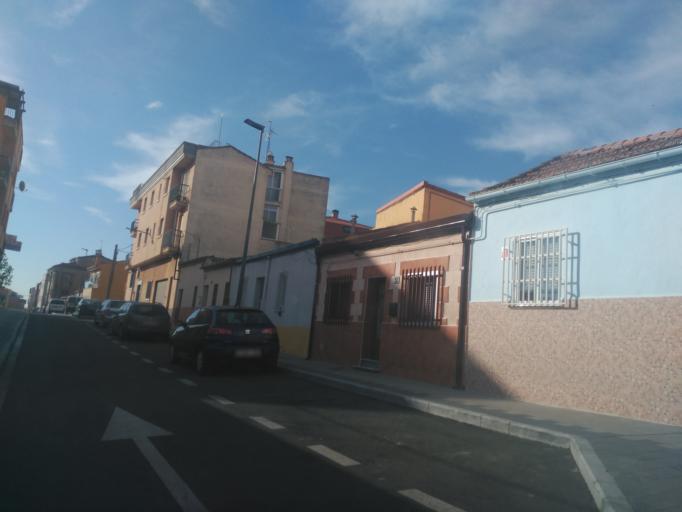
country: ES
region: Castille and Leon
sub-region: Provincia de Salamanca
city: Salamanca
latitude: 40.9787
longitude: -5.6781
